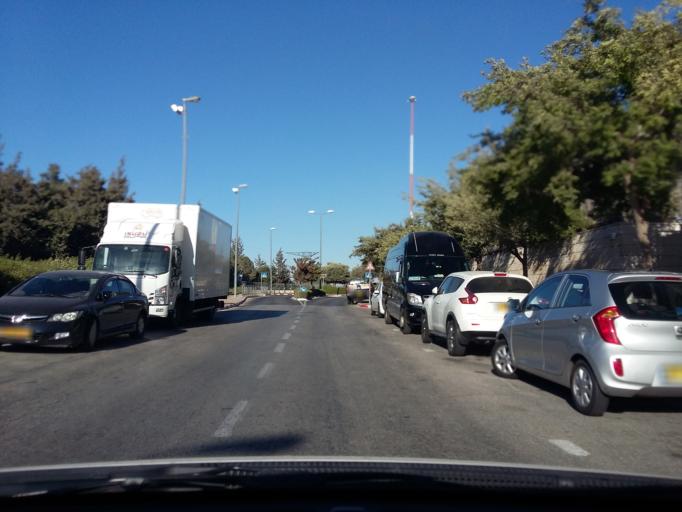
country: PS
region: West Bank
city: `Anata
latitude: 31.8074
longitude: 35.2389
